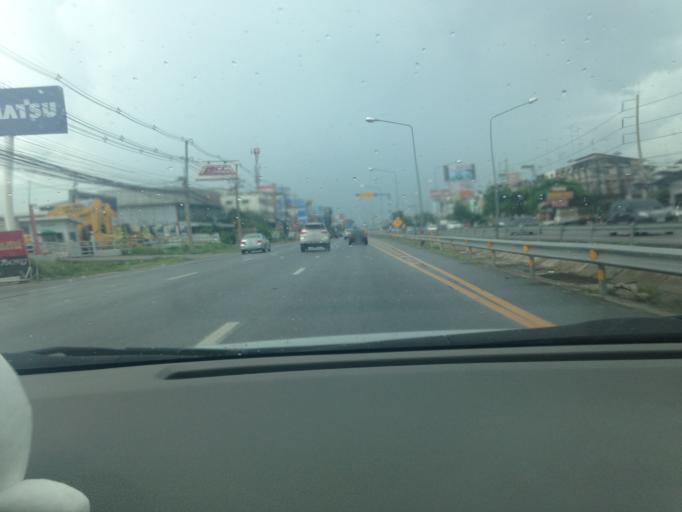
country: TH
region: Chon Buri
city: Chon Buri
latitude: 13.3046
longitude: 100.9509
